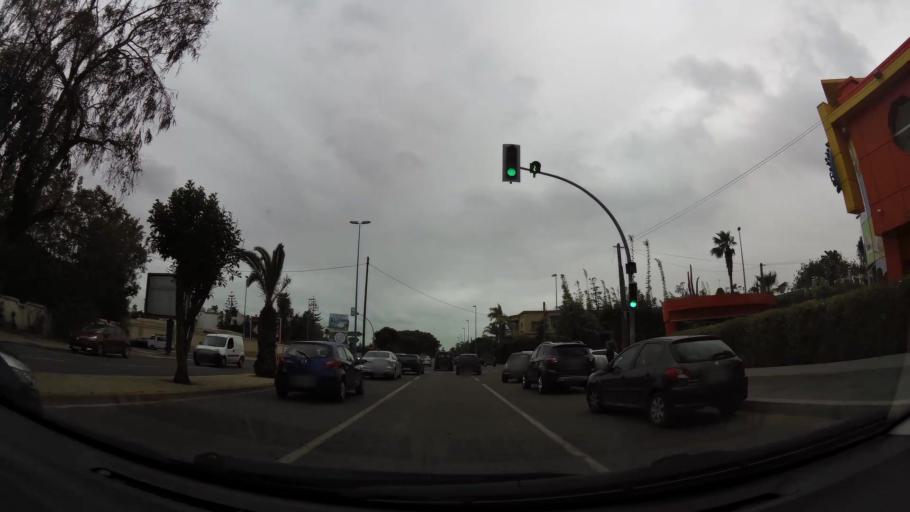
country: MA
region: Grand Casablanca
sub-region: Casablanca
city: Casablanca
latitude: 33.5938
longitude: -7.6545
